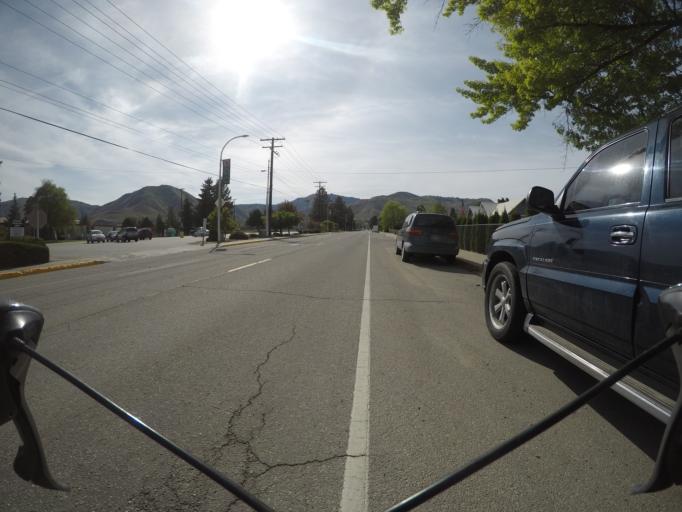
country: US
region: Washington
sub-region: Chelan County
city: West Wenatchee
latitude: 47.4327
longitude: -120.3366
